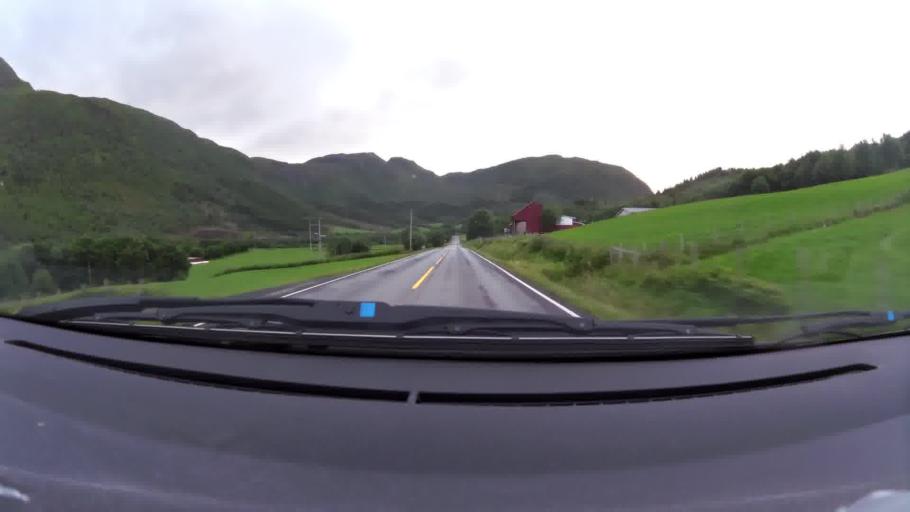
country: NO
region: More og Romsdal
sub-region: Molde
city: Molde
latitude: 62.7926
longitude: 7.2502
